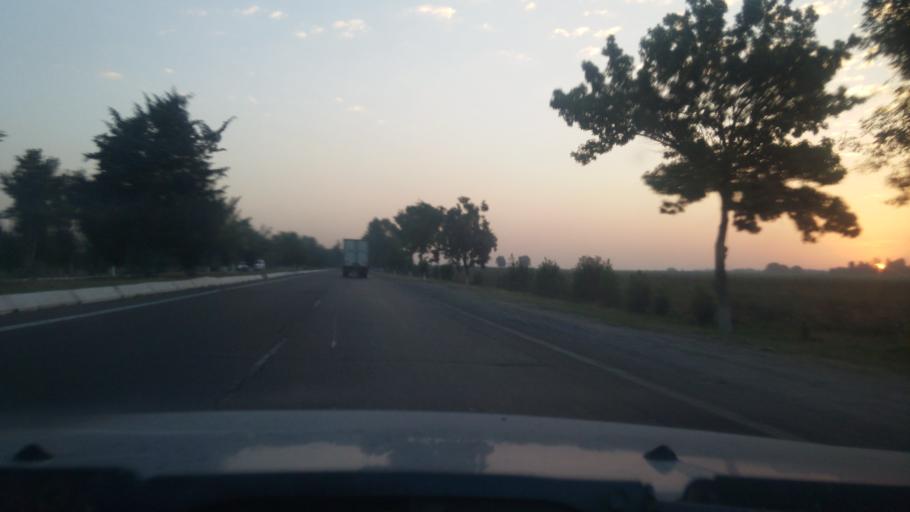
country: UZ
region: Toshkent
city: Chinoz
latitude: 40.9990
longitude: 68.8197
